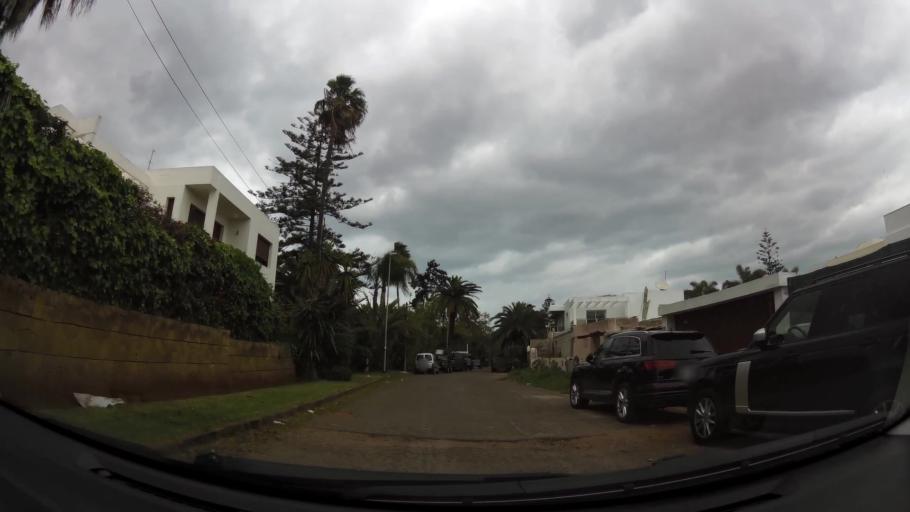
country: MA
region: Grand Casablanca
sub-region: Casablanca
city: Casablanca
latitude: 33.5794
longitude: -7.6606
